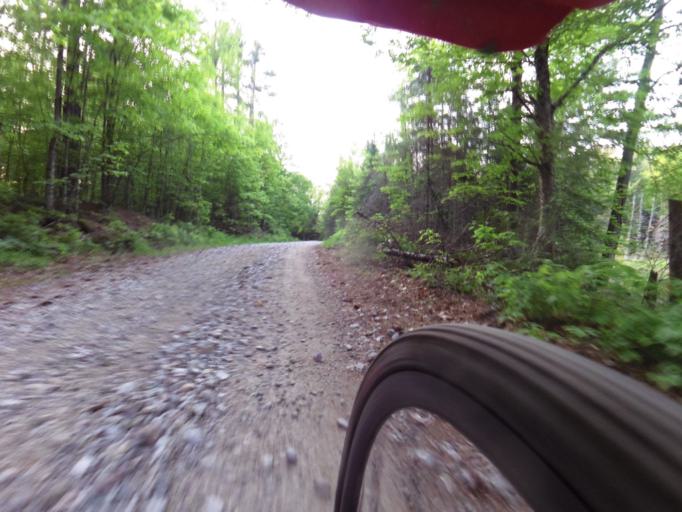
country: CA
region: Ontario
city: Arnprior
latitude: 45.1829
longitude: -76.5053
